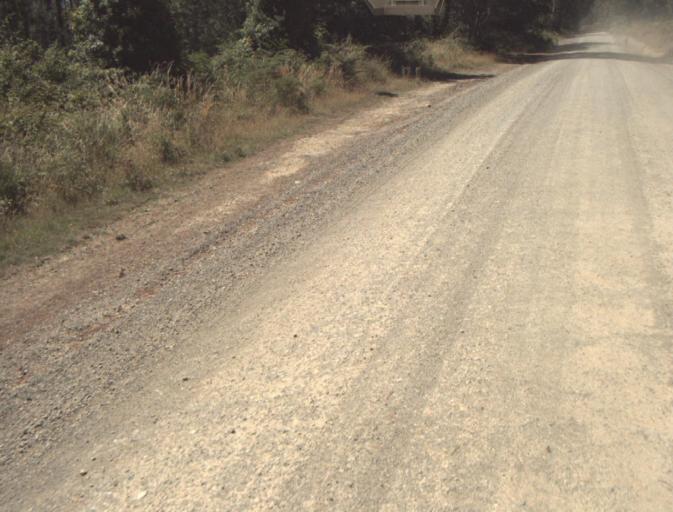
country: AU
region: Tasmania
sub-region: Dorset
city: Scottsdale
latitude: -41.3388
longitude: 147.4315
